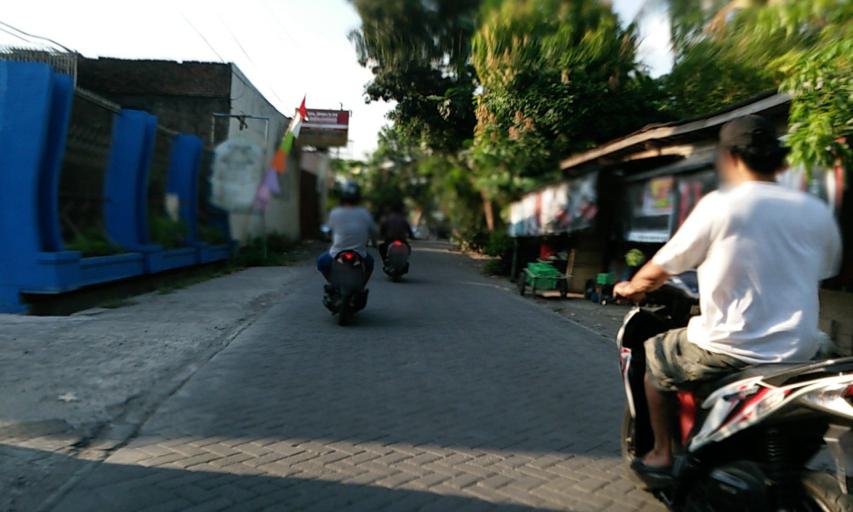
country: ID
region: Central Java
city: Mranggen
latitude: -7.0108
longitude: 110.4875
